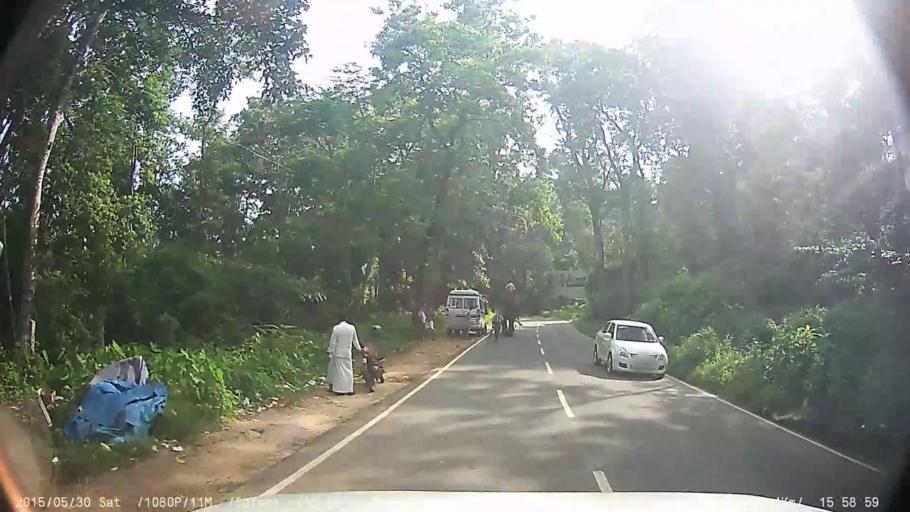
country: IN
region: Kerala
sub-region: Wayanad
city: Kalpetta
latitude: 11.6470
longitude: 76.0894
